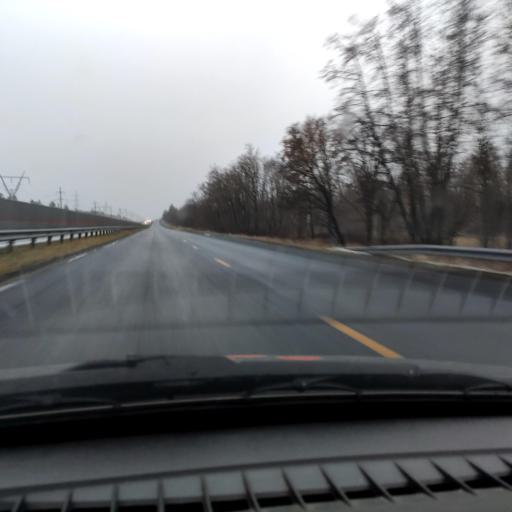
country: RU
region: Samara
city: Pribrezhnyy
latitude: 53.5149
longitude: 49.8836
